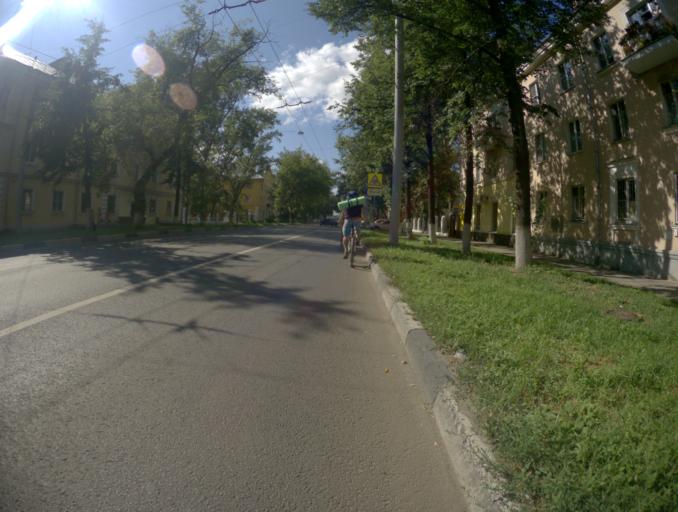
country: RU
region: Nizjnij Novgorod
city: Nizhniy Novgorod
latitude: 56.3256
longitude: 43.9559
